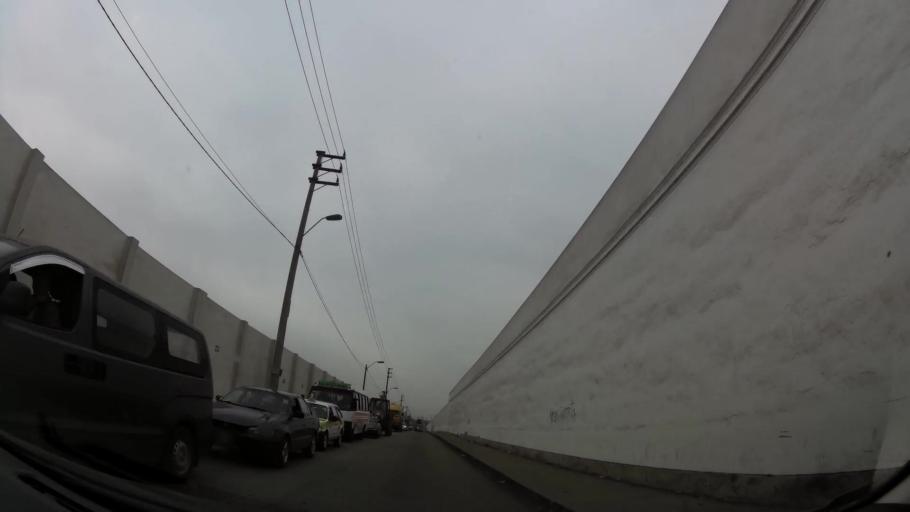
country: PE
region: Lima
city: Lima
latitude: -12.0413
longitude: -77.0050
